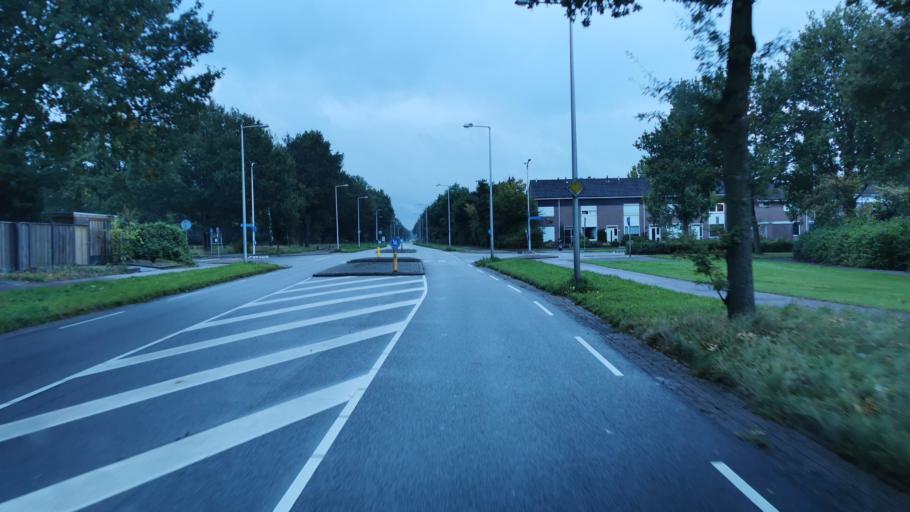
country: NL
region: Overijssel
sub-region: Gemeente Enschede
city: Enschede
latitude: 52.1909
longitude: 6.9023
